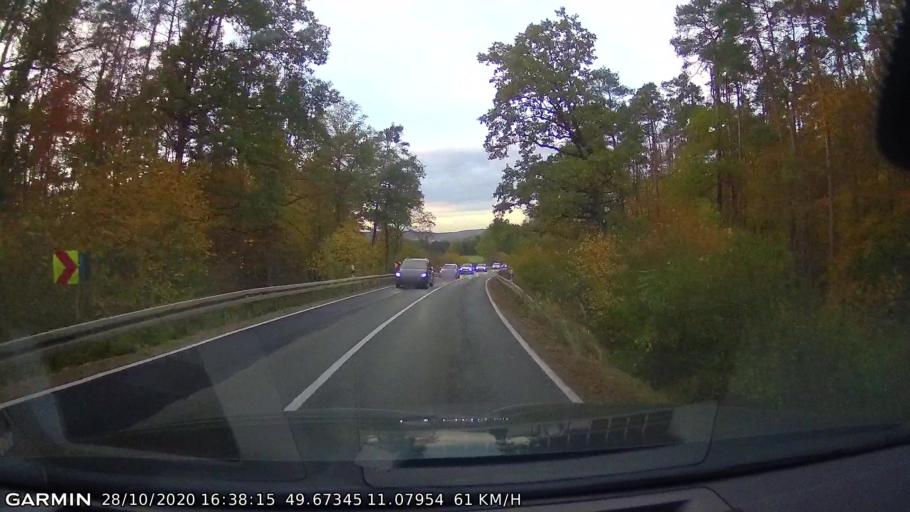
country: DE
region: Bavaria
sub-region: Upper Franconia
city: Poxdorf
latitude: 49.6736
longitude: 11.0794
